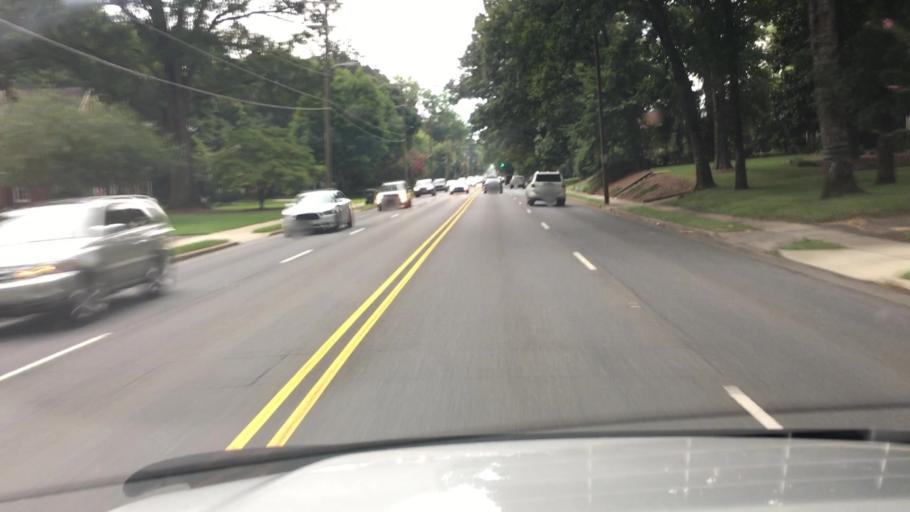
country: US
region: North Carolina
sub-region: Mecklenburg County
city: Charlotte
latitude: 35.1910
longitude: -80.8235
